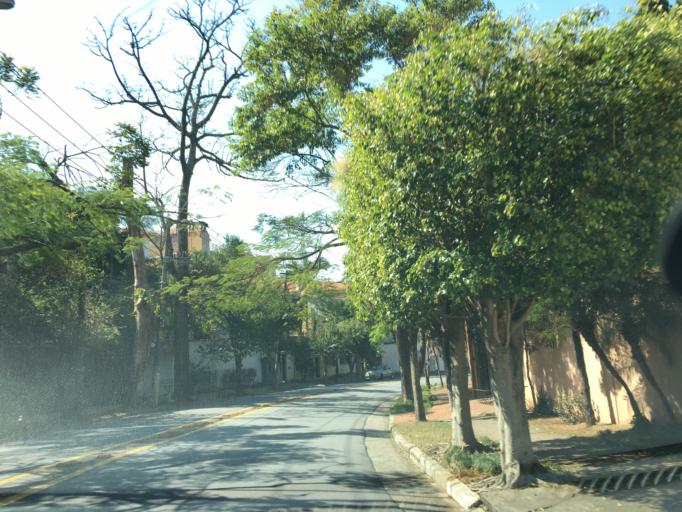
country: BR
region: Sao Paulo
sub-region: Sao Paulo
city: Sao Paulo
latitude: -23.5396
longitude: -46.6674
